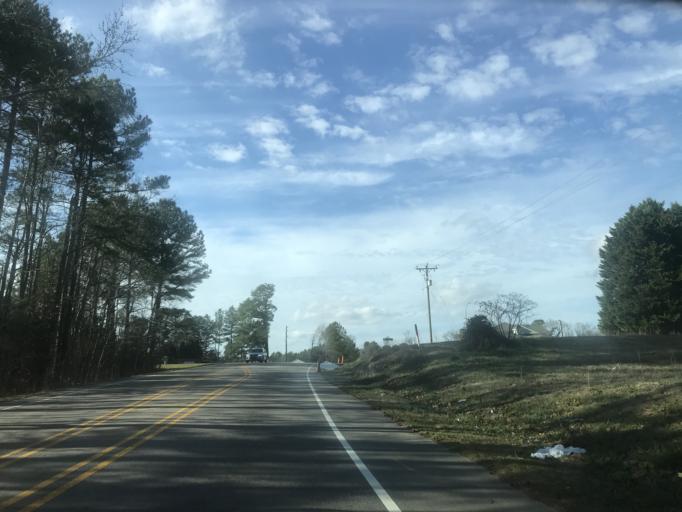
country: US
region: North Carolina
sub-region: Wake County
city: Garner
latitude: 35.7278
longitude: -78.5525
